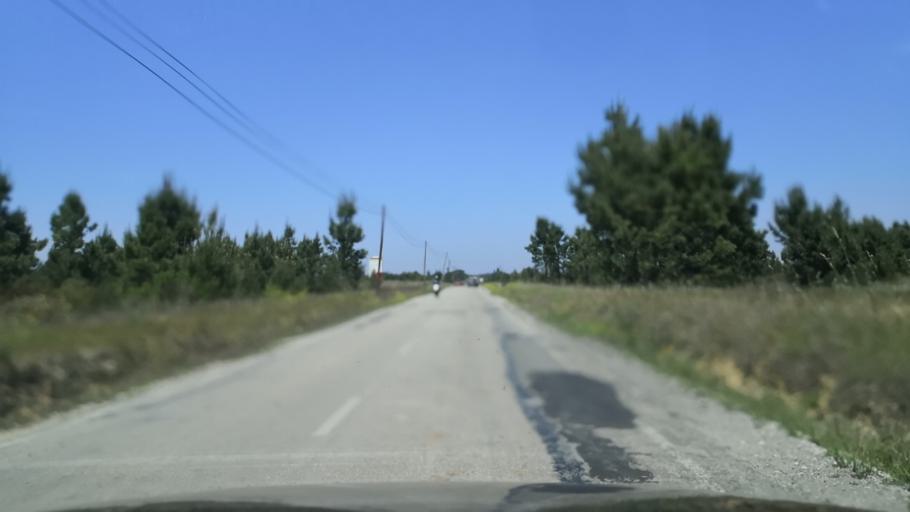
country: PT
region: Setubal
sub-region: Palmela
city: Palmela
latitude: 38.6254
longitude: -8.7466
